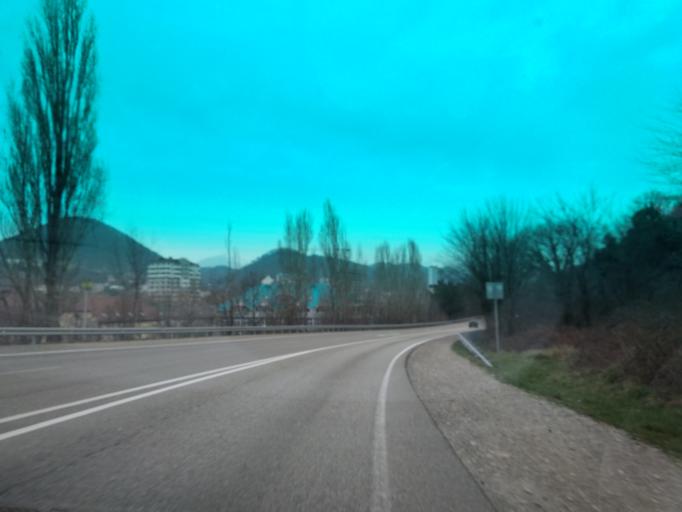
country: RU
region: Krasnodarskiy
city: Ol'ginka
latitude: 44.1909
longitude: 38.8889
